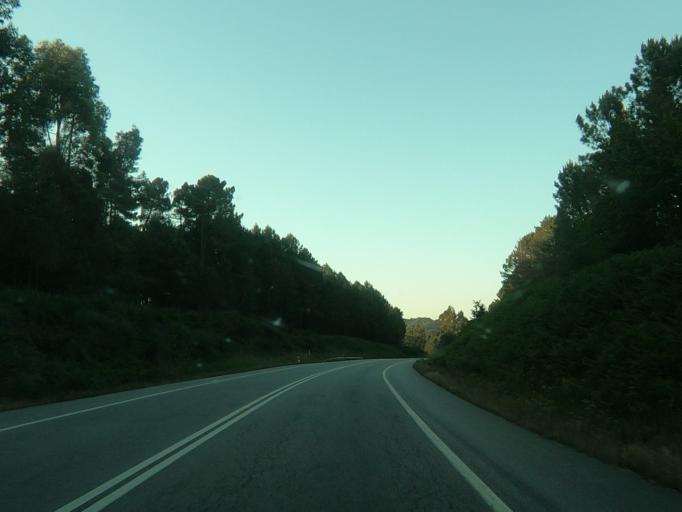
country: PT
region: Viseu
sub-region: Viseu
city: Rio de Loba
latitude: 40.6663
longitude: -7.8617
